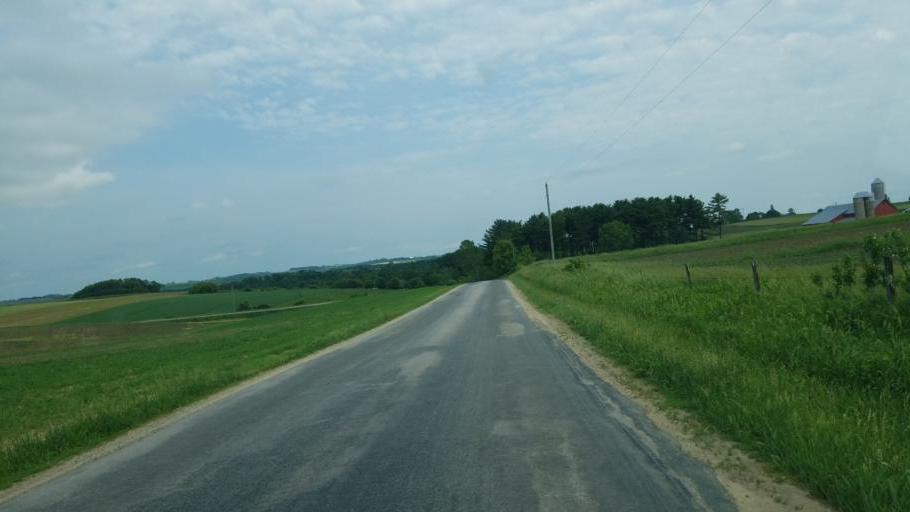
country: US
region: Wisconsin
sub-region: Monroe County
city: Cashton
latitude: 43.7126
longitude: -90.7103
